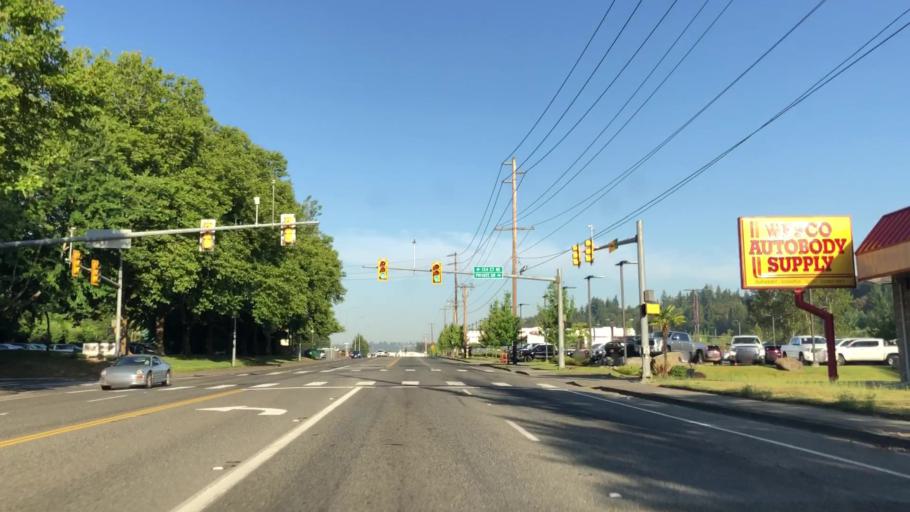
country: US
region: Washington
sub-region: King County
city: Kingsgate
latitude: 47.7114
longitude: -122.1612
